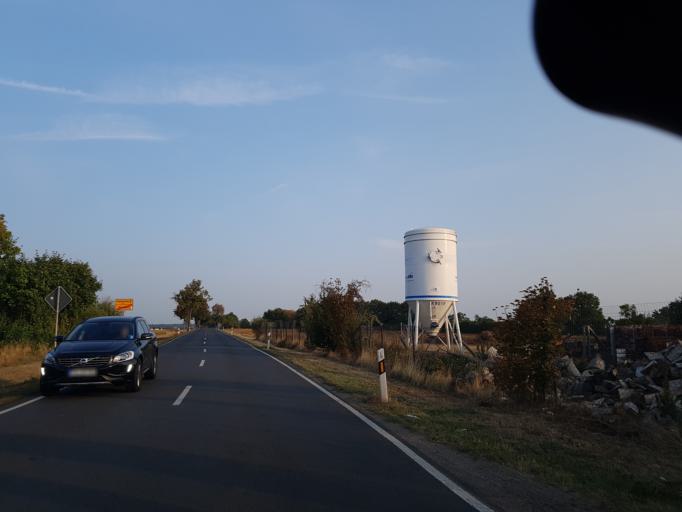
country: DE
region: Saxony
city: Elsnig
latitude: 51.5971
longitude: 12.9456
